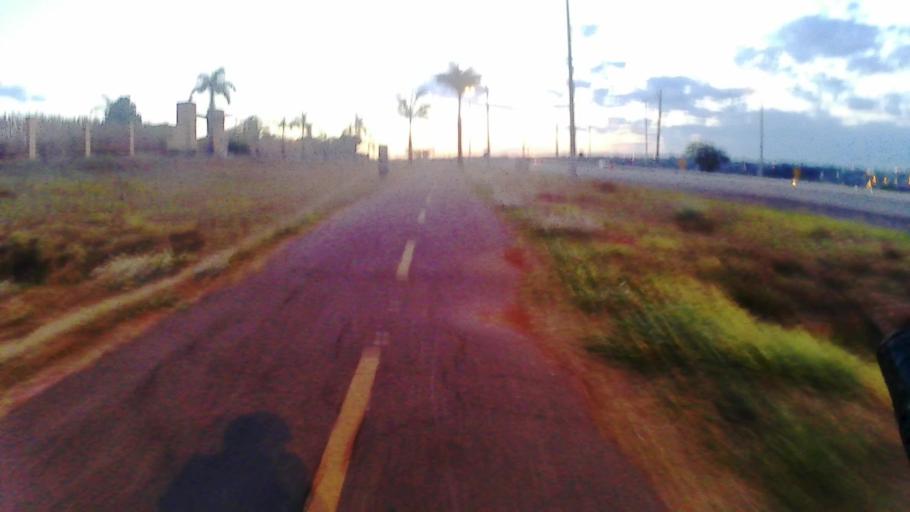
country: BR
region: Federal District
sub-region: Brasilia
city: Brasilia
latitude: -15.8679
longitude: -47.9890
